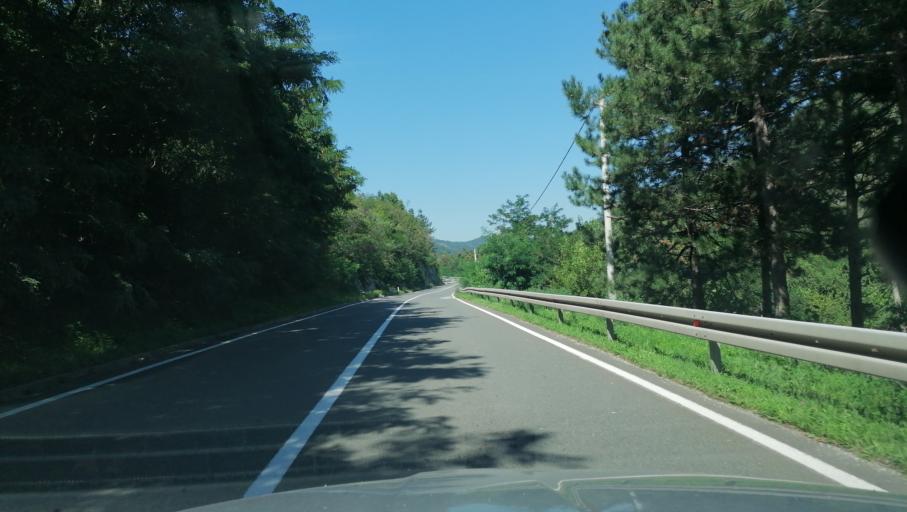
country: RS
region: Central Serbia
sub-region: Raski Okrug
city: Kraljevo
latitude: 43.6378
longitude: 20.5505
